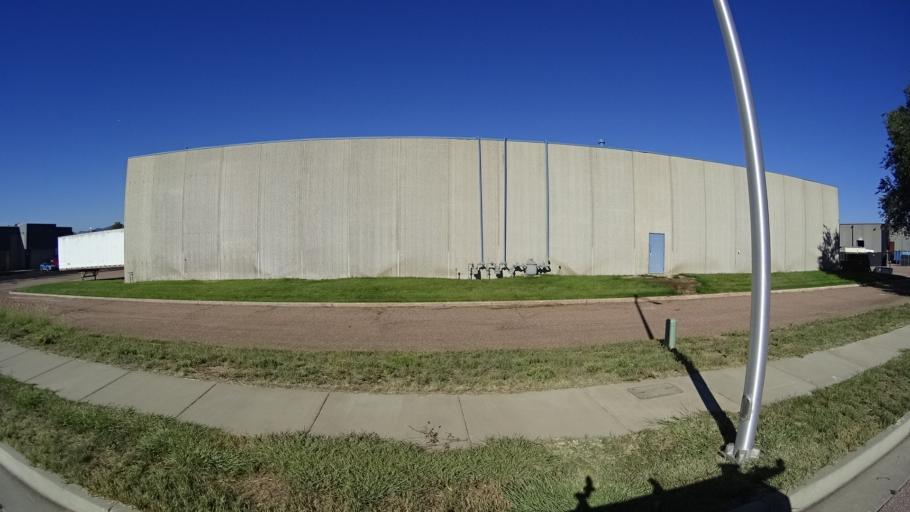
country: US
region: Colorado
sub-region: El Paso County
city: Cimarron Hills
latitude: 38.8116
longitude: -104.7238
